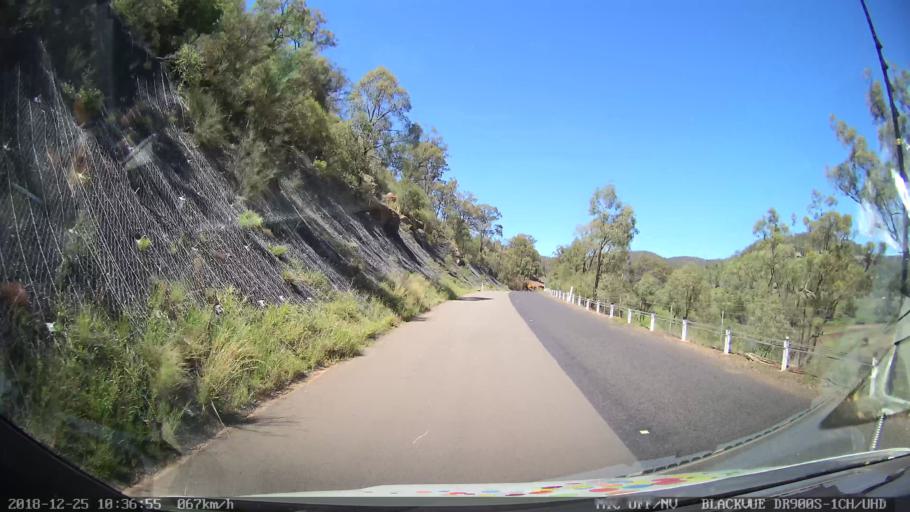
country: AU
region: New South Wales
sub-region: Upper Hunter Shire
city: Merriwa
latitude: -32.4089
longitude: 150.3829
